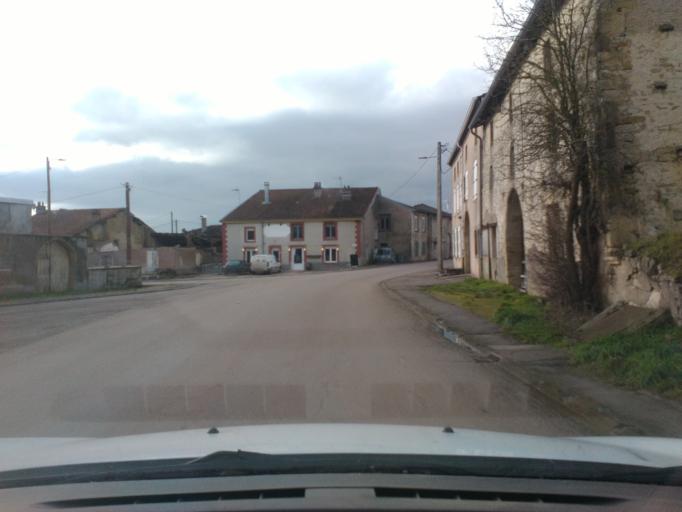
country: FR
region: Lorraine
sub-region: Departement des Vosges
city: Mirecourt
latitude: 48.3352
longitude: 6.0212
